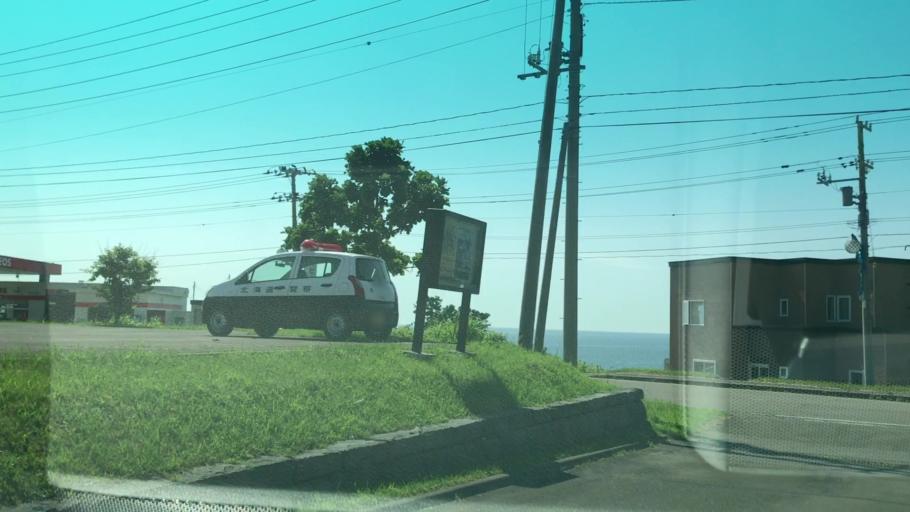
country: JP
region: Hokkaido
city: Iwanai
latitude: 43.0624
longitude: 140.4980
